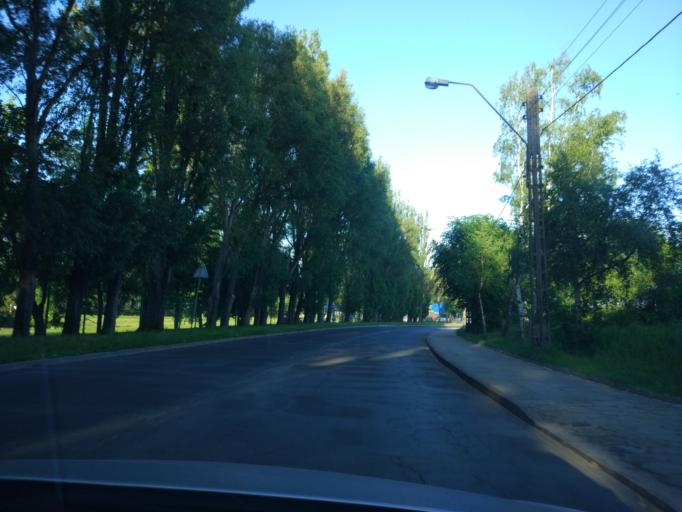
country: PL
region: Lodz Voivodeship
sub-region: Powiat kutnowski
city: Kutno
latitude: 52.2252
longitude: 19.3589
